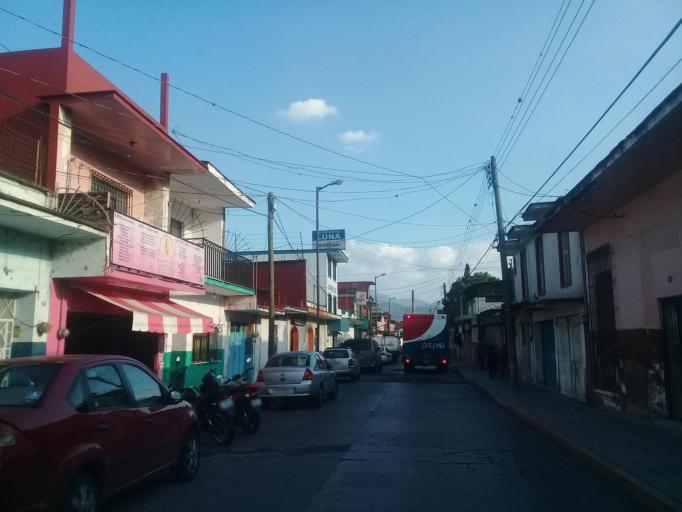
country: MX
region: Veracruz
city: Orizaba
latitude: 18.8542
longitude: -97.1083
